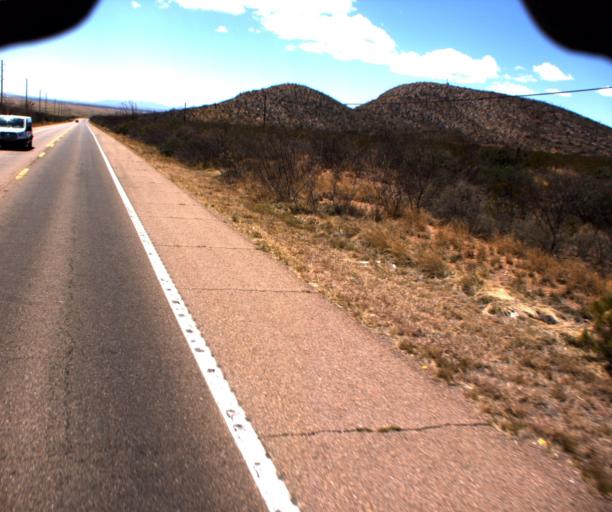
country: US
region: Arizona
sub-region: Cochise County
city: Naco
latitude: 31.3777
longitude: -109.9658
